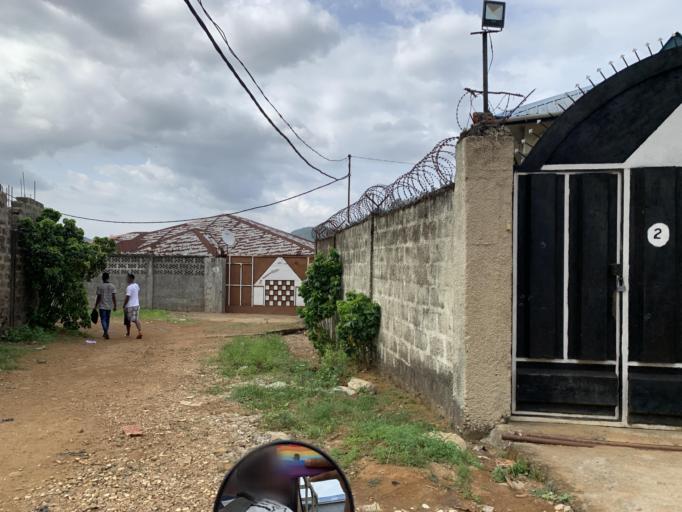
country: SL
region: Western Area
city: Hastings
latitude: 8.3906
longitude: -13.1492
